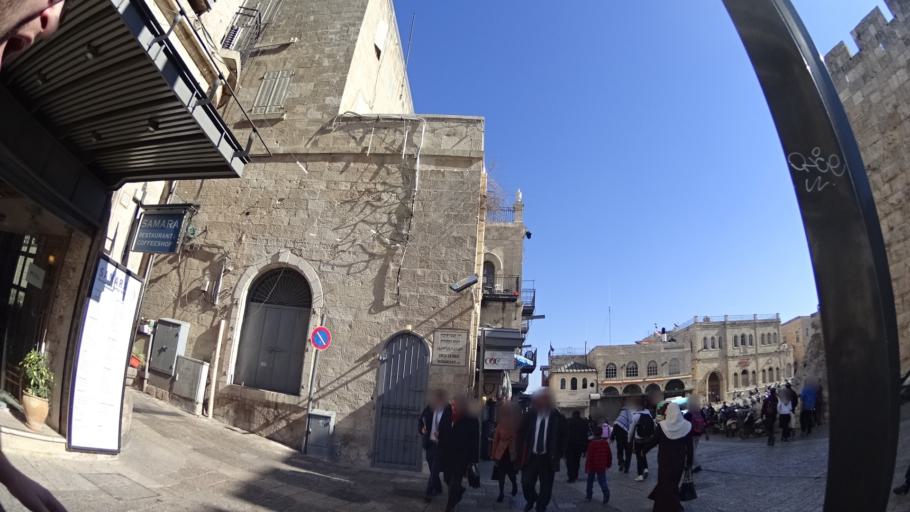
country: PS
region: West Bank
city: Old City
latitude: 31.7767
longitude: 35.2287
